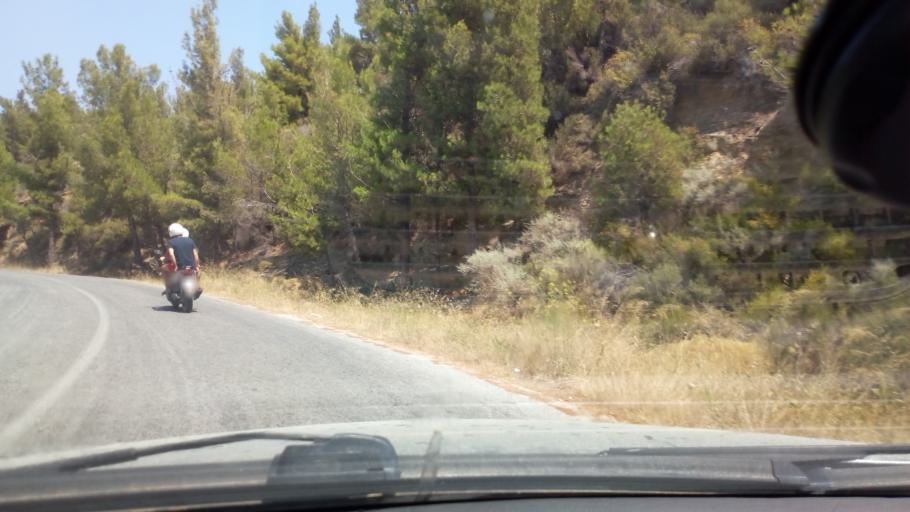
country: GR
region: North Aegean
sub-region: Nomos Samou
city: Agios Kirykos
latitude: 37.6302
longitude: 26.1415
